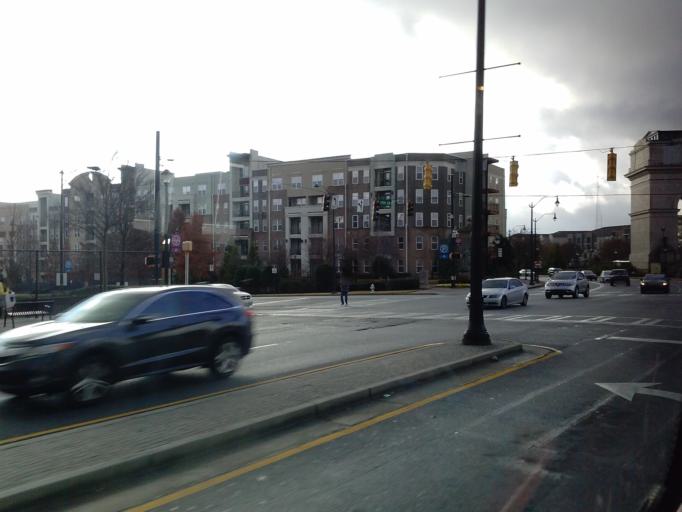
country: US
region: Georgia
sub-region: Fulton County
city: Atlanta
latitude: 33.7912
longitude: -84.3986
